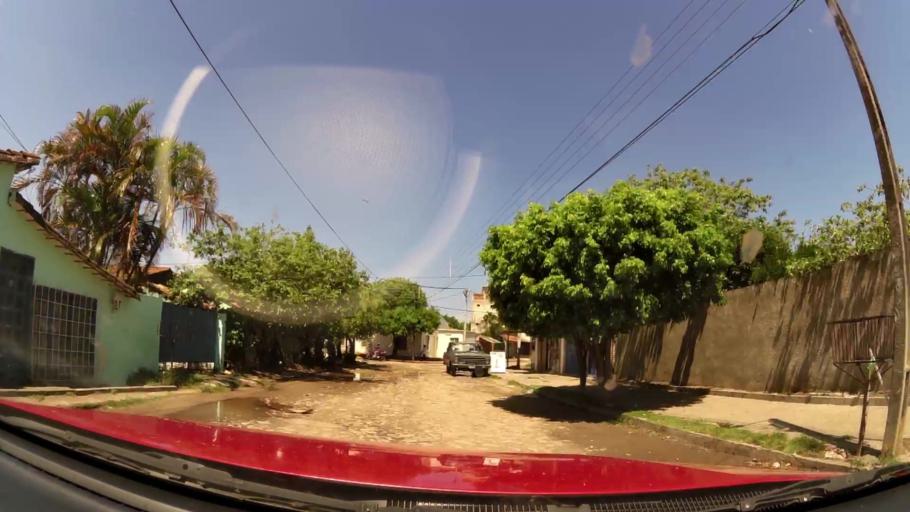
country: PY
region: Central
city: Colonia Mariano Roque Alonso
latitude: -25.2486
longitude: -57.5539
